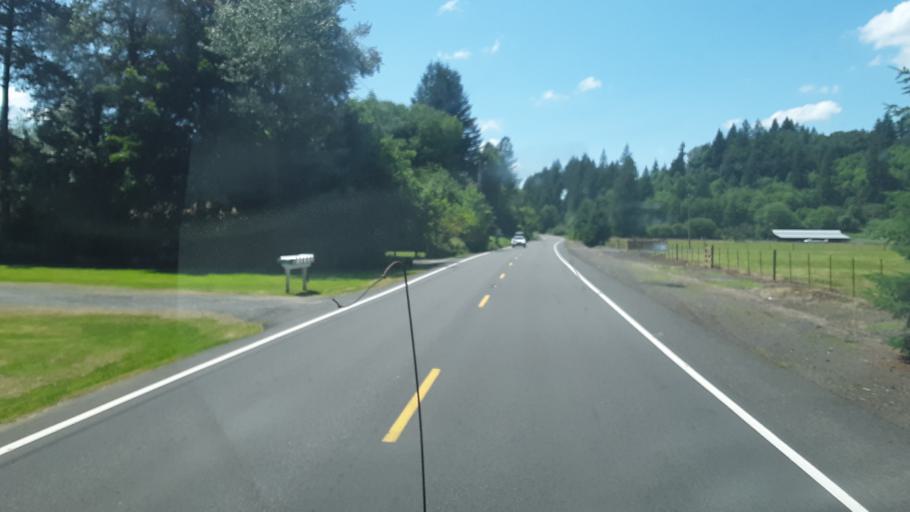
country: US
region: Washington
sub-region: Clark County
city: Yacolt
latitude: 45.9242
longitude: -122.3847
